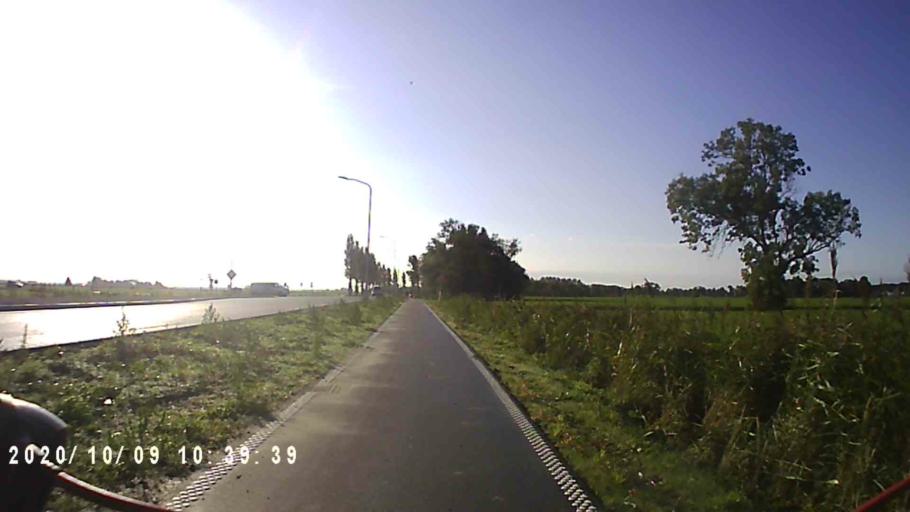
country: NL
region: Groningen
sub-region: Gemeente Winsum
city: Winsum
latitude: 53.2840
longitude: 6.5345
